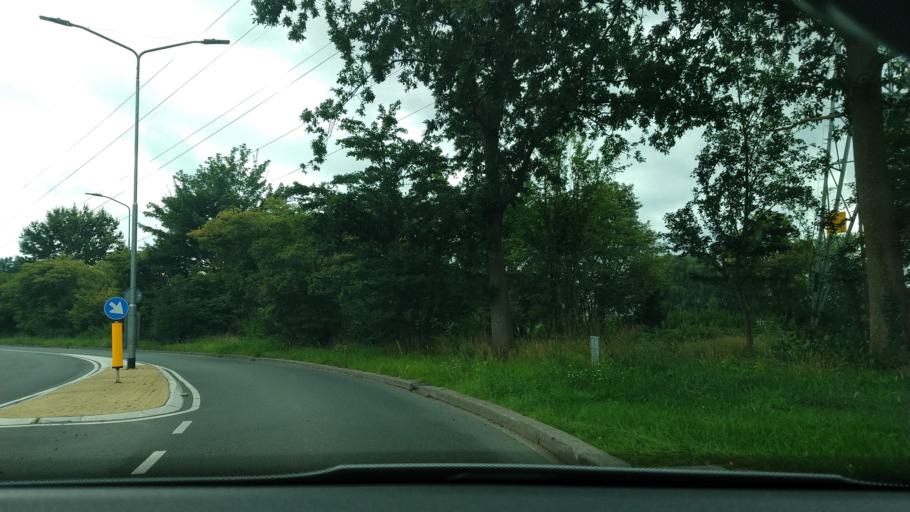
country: NL
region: Gelderland
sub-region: Gemeente Ermelo
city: Horst
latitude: 52.3020
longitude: 5.5987
